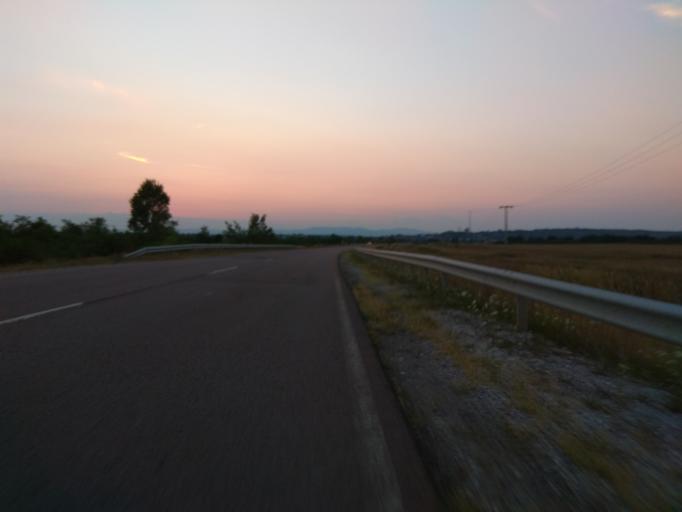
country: HU
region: Borsod-Abauj-Zemplen
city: Emod
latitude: 47.9257
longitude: 20.8364
